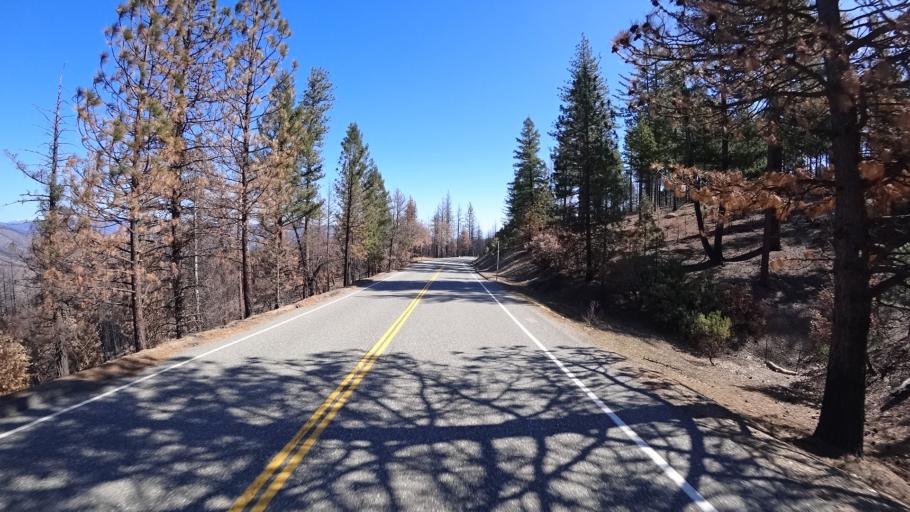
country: US
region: California
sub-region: Tehama County
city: Rancho Tehama Reserve
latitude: 39.6525
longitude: -122.7331
